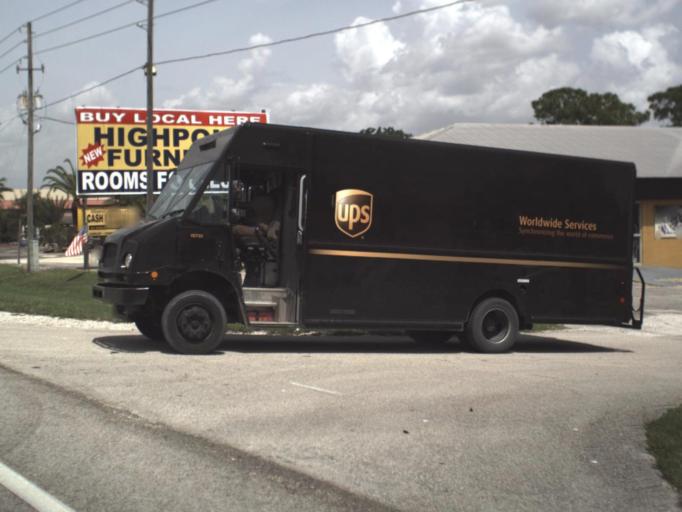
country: US
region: Florida
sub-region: Highlands County
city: Sebring
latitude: 27.5052
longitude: -81.4914
